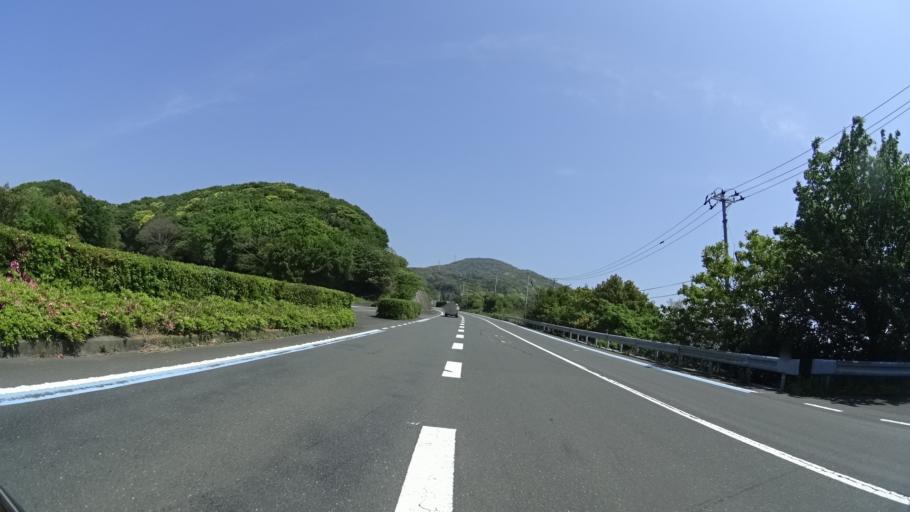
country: JP
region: Ehime
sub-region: Nishiuwa-gun
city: Ikata-cho
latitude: 33.4053
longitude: 132.1717
